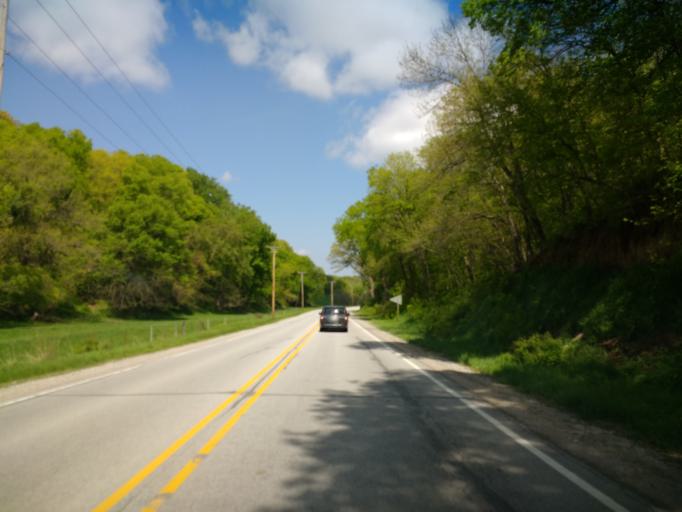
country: US
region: Iowa
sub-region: Harrison County
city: Missouri Valley
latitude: 41.4272
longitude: -95.8551
